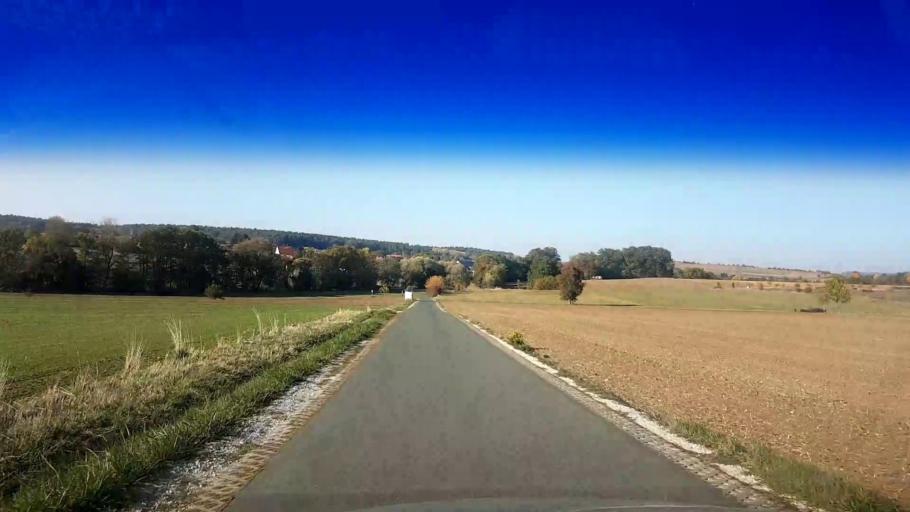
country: DE
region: Bavaria
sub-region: Upper Franconia
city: Strullendorf
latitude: 49.8599
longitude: 10.9990
